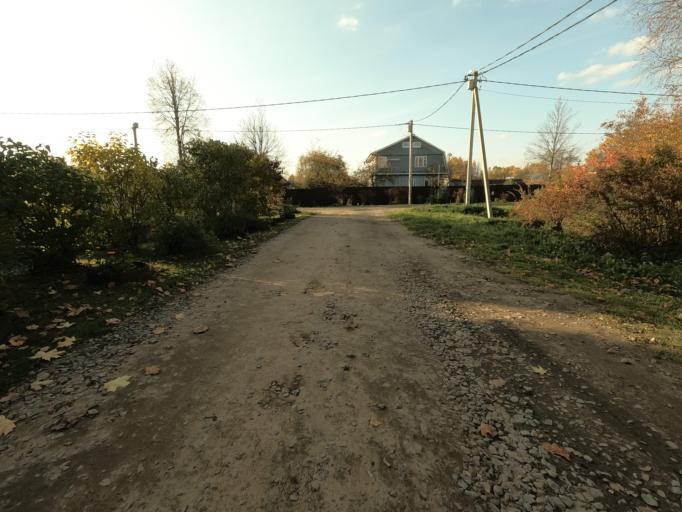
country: RU
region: Leningrad
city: Mga
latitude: 59.7542
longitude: 31.0512
